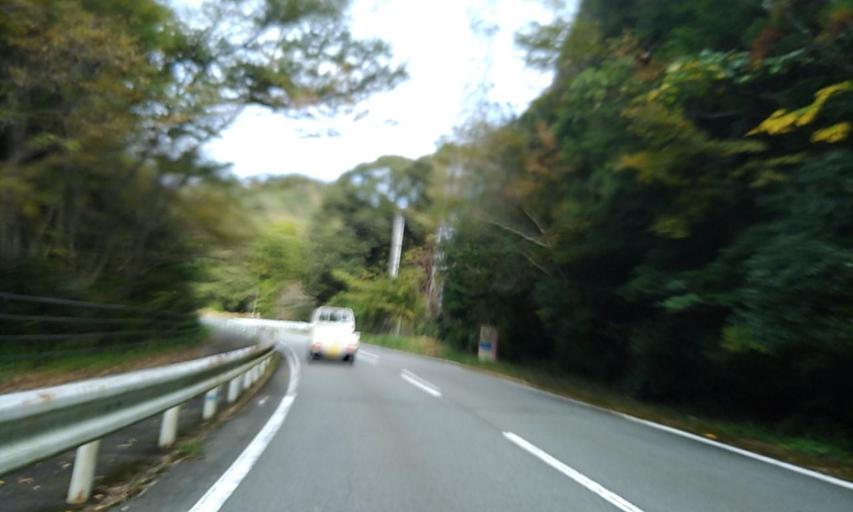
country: JP
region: Mie
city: Ise
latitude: 34.2948
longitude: 136.6016
